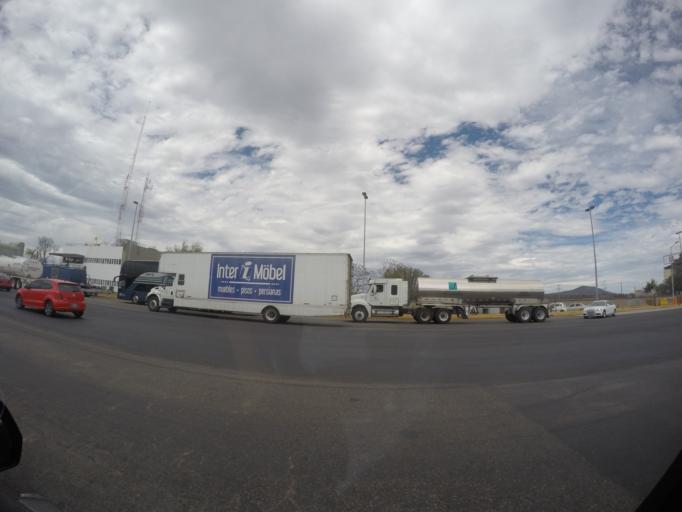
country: MX
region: Queretaro
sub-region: San Juan del Rio
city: Paso de Mata
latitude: 20.2945
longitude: -99.9259
